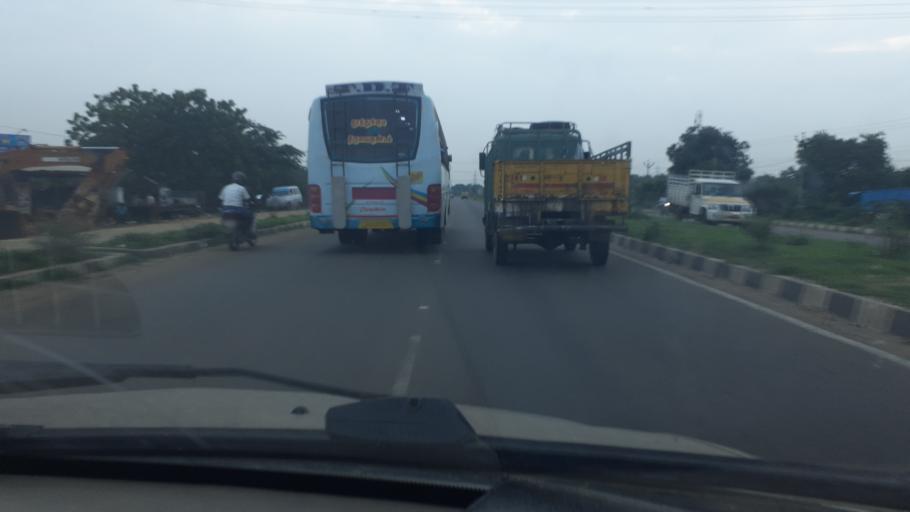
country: IN
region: Tamil Nadu
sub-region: Thoothukkudi
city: Korampallam
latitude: 8.7759
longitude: 78.0890
